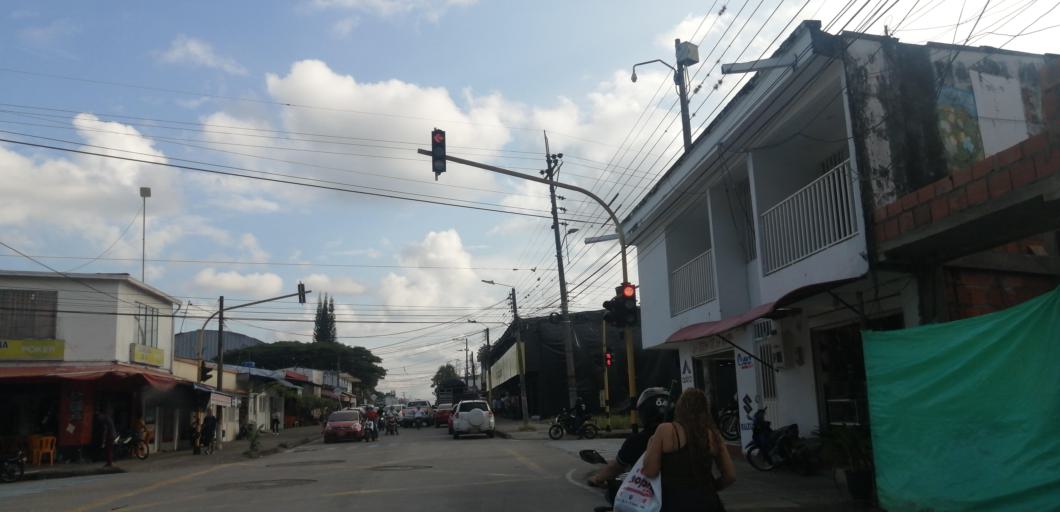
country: CO
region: Meta
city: Acacias
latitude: 3.9843
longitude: -73.7628
